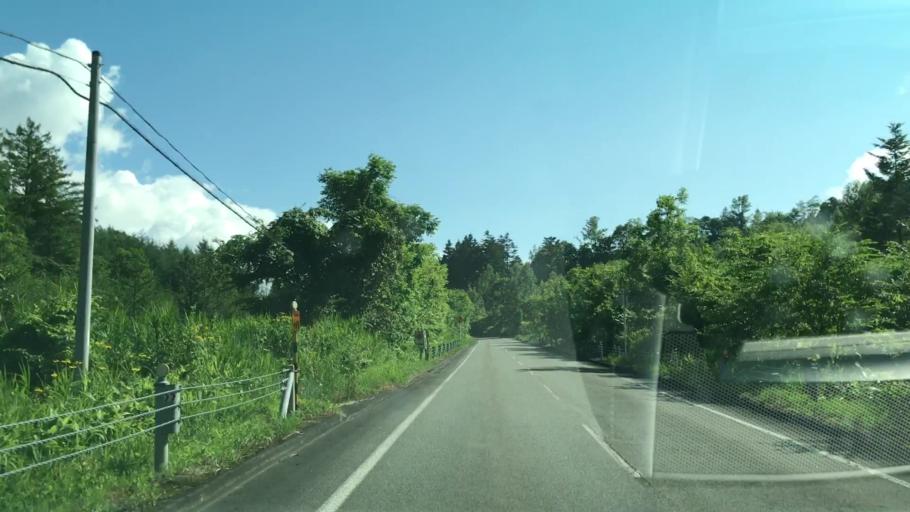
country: JP
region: Hokkaido
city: Shimo-furano
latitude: 42.8626
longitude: 142.4409
